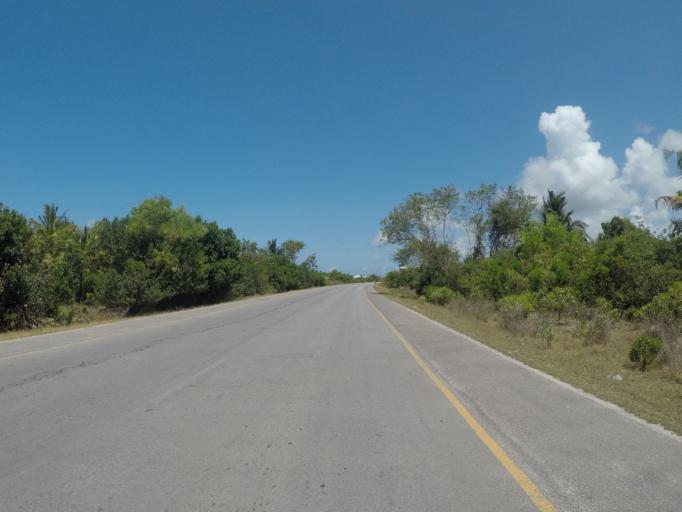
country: TZ
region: Zanzibar Central/South
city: Nganane
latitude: -6.3107
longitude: 39.5412
